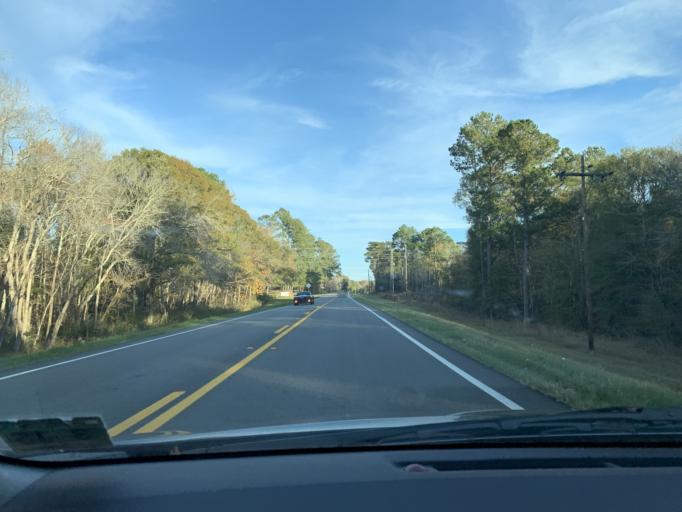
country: US
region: Georgia
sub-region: Irwin County
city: Ocilla
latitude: 31.5954
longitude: -83.1229
